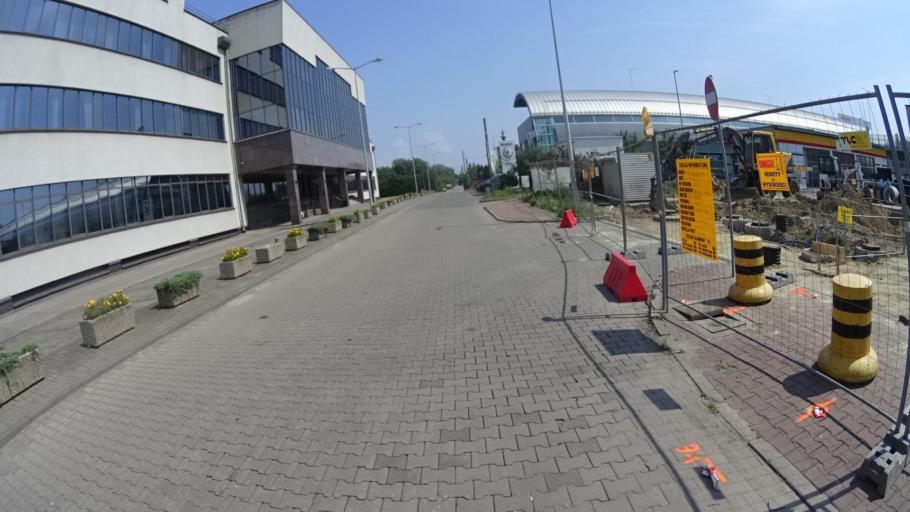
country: PL
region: Masovian Voivodeship
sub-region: Warszawa
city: Ursynow
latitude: 52.1407
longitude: 21.0194
